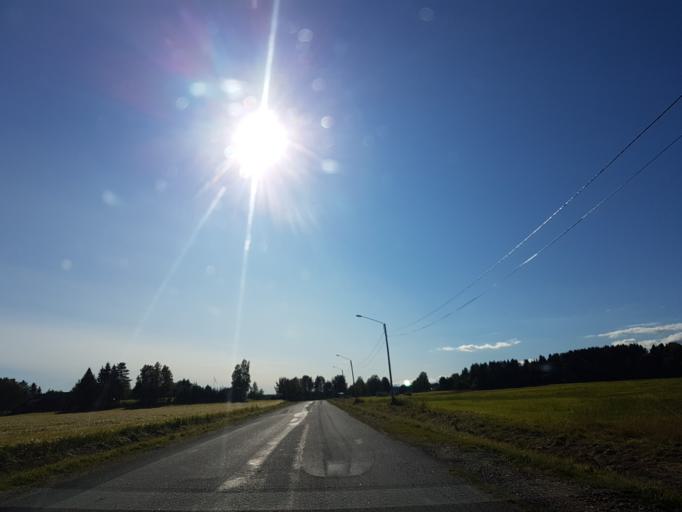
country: SE
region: Vaesterbotten
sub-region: Skelleftea Kommun
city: Burea
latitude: 64.3912
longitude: 21.3235
